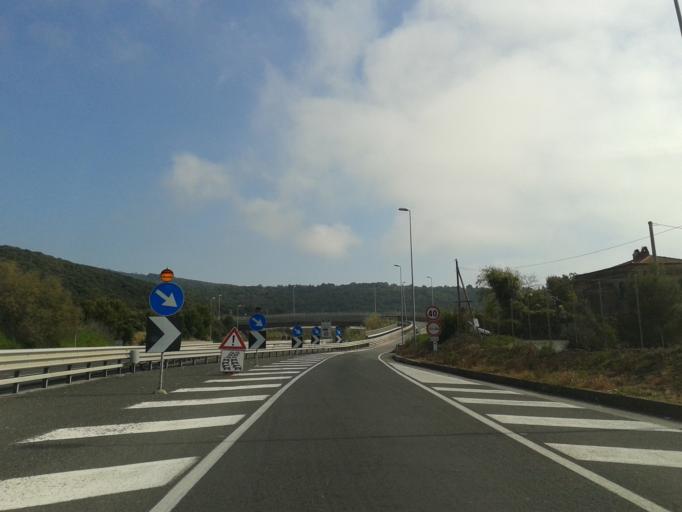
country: IT
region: Tuscany
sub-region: Provincia di Livorno
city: Quercianella
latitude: 43.4854
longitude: 10.3330
